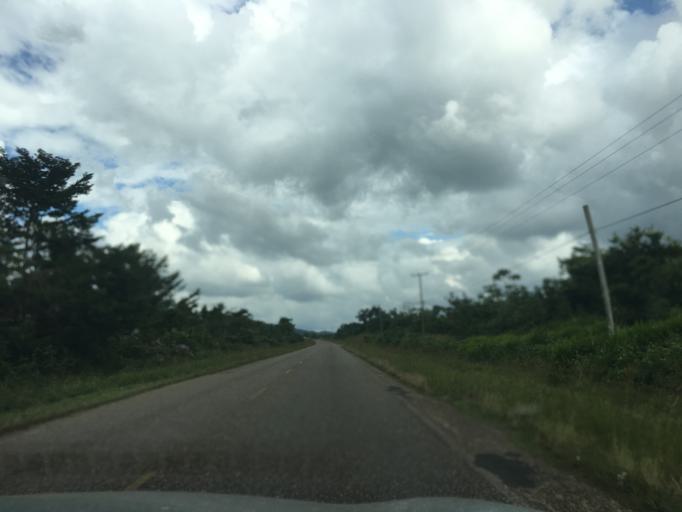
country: BZ
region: Stann Creek
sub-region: Dangriga
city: Dangriga
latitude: 16.9137
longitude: -88.3422
